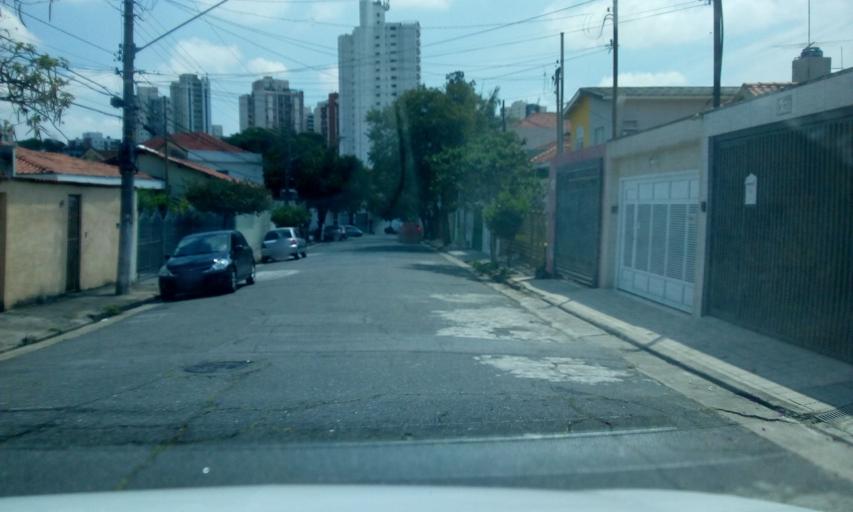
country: BR
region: Sao Paulo
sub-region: Sao Paulo
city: Sao Paulo
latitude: -23.5339
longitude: -46.7006
